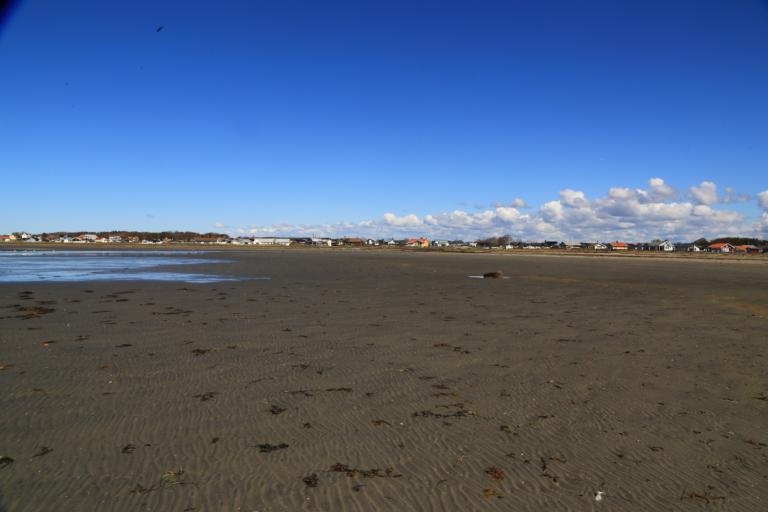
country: SE
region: Halland
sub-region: Varbergs Kommun
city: Traslovslage
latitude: 57.0664
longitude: 12.2748
